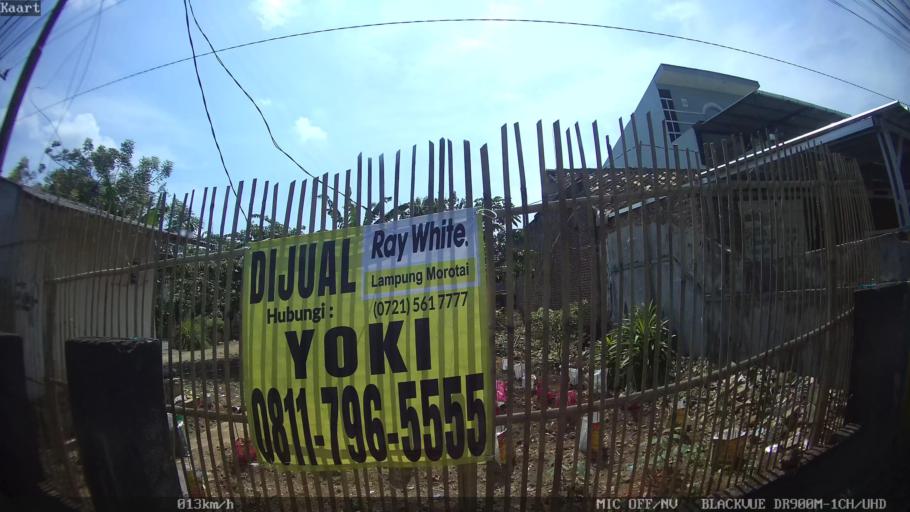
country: ID
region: Lampung
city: Kedaton
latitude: -5.3738
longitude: 105.2598
